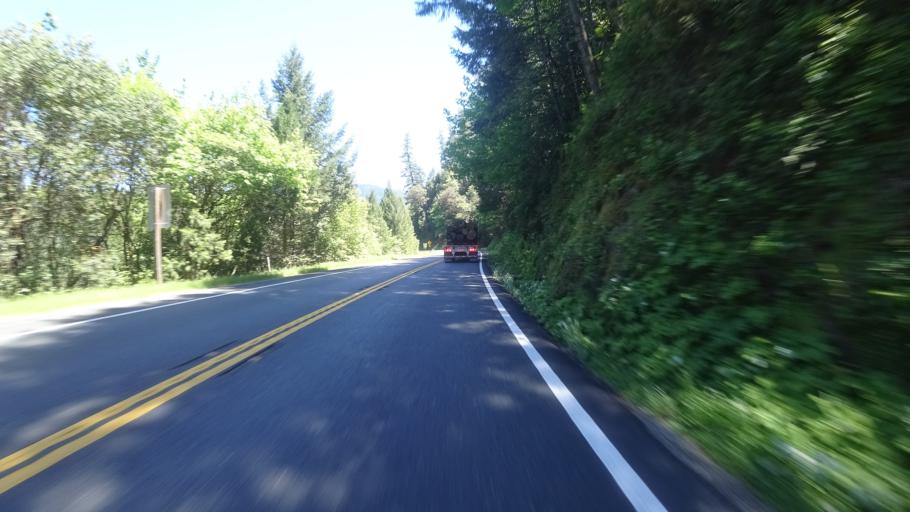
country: US
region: California
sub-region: Humboldt County
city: Willow Creek
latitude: 40.9455
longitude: -123.6548
